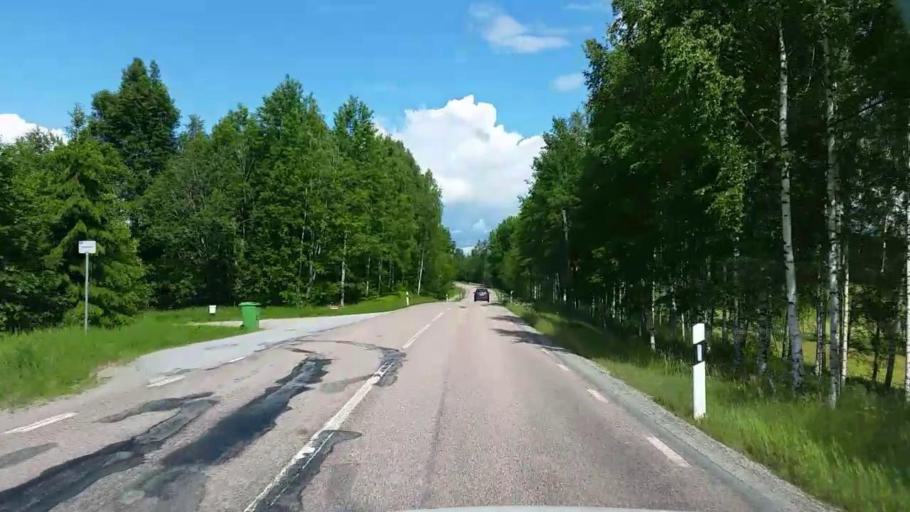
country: SE
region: Vaestmanland
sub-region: Fagersta Kommun
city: Fagersta
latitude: 59.9319
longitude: 15.8264
